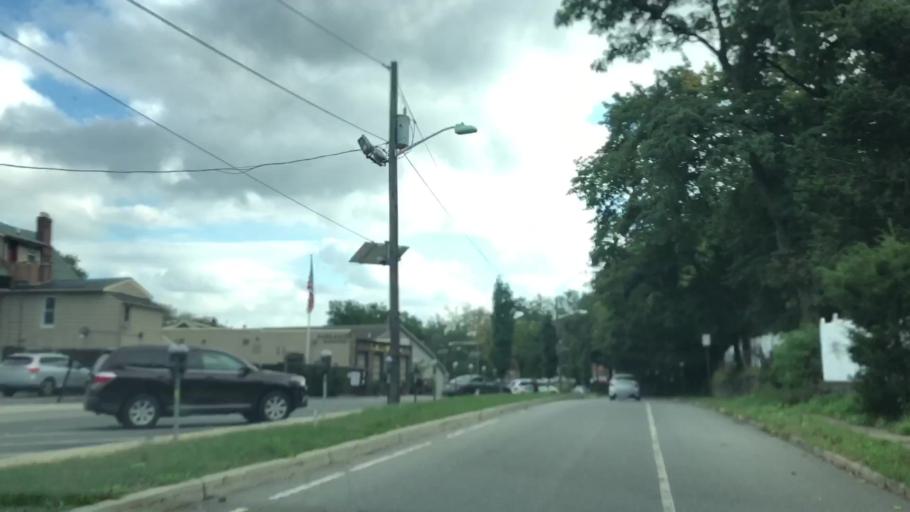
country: US
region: New Jersey
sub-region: Essex County
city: Glen Ridge
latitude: 40.7975
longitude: -74.2197
